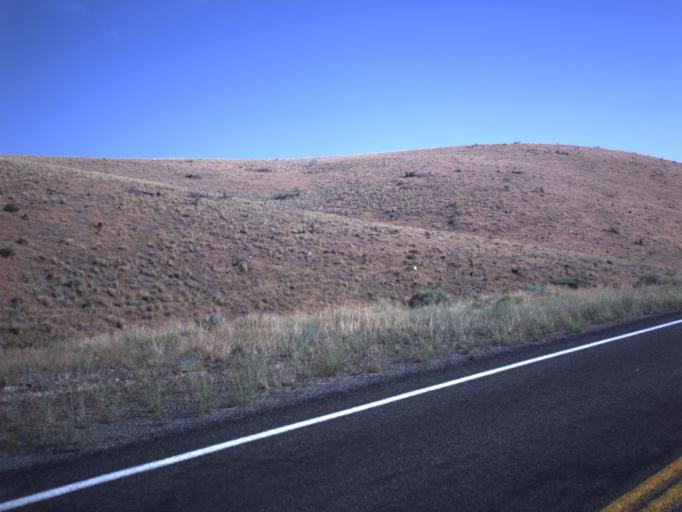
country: US
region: Utah
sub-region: Iron County
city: Parowan
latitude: 38.0833
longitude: -112.9567
